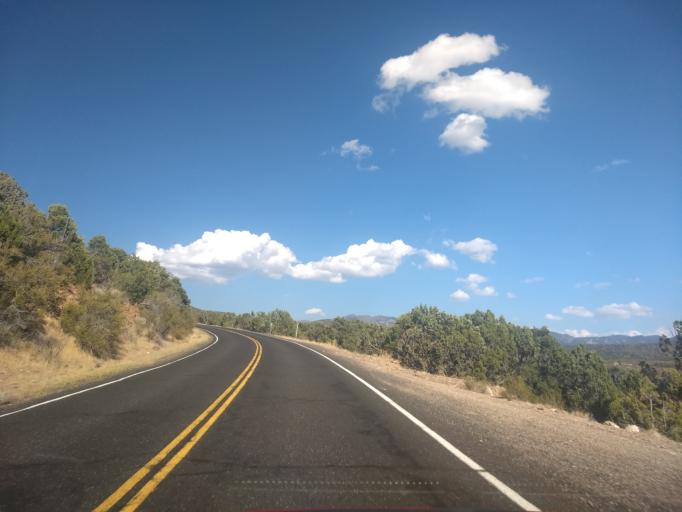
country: US
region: Utah
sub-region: Washington County
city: Enterprise
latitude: 37.4160
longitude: -113.5661
